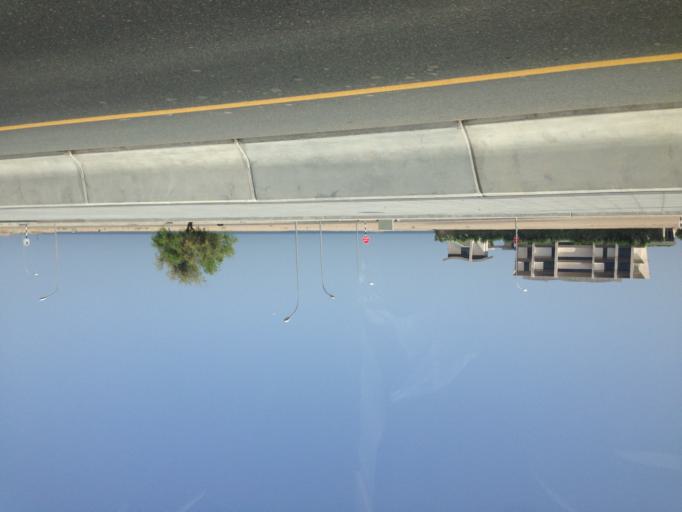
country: OM
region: Muhafazat Masqat
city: Bawshar
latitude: 23.6076
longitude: 58.3148
